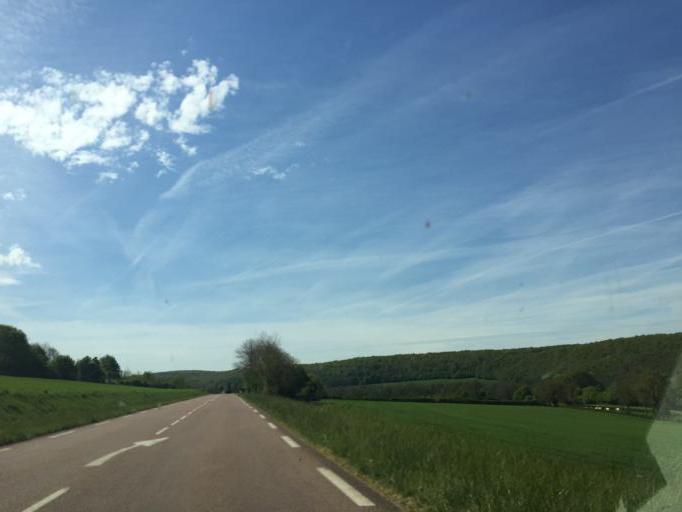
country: FR
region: Bourgogne
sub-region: Departement de la Nievre
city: Clamecy
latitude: 47.4390
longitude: 3.5580
